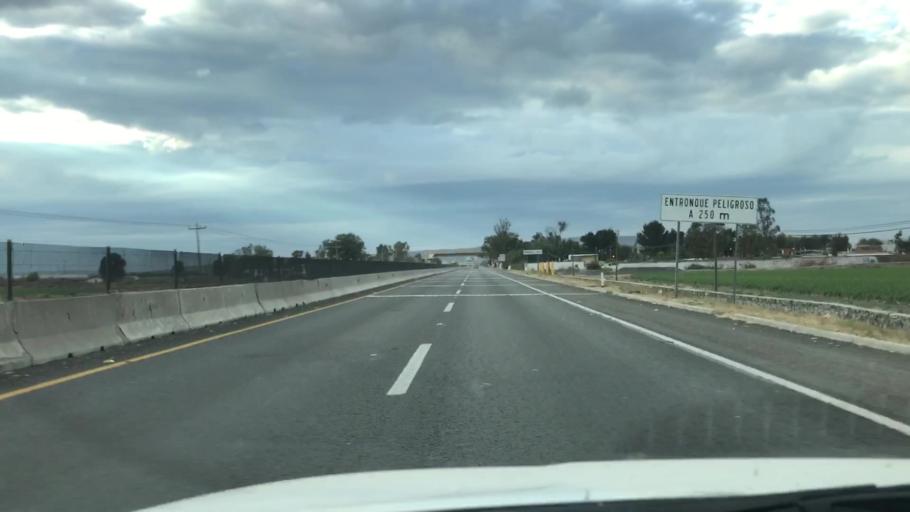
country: MX
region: Guanajuato
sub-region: Penjamo
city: Estacion la Piedad
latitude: 20.3875
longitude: -101.9174
